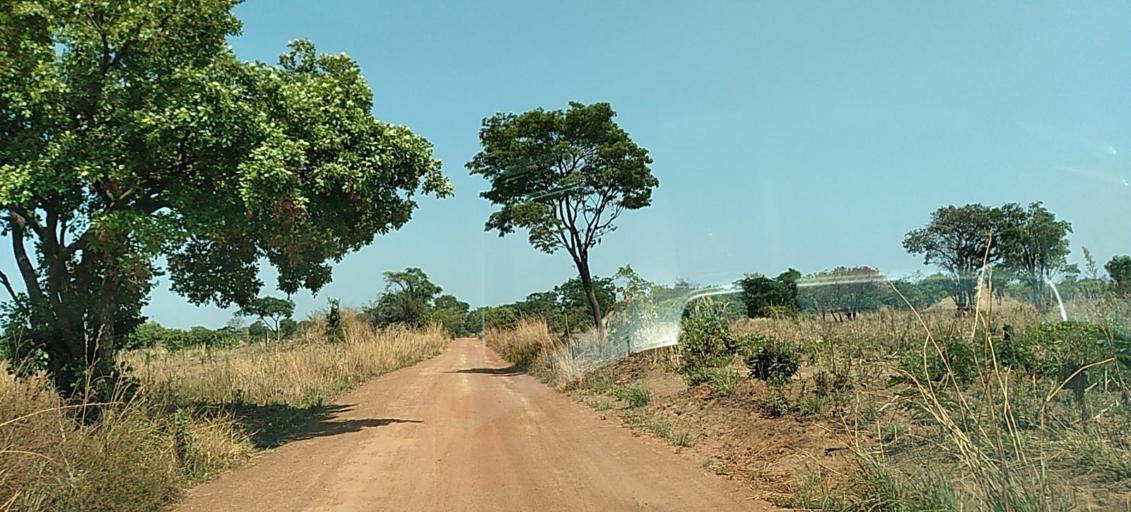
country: ZM
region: Copperbelt
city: Chingola
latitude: -12.5428
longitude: 27.7418
